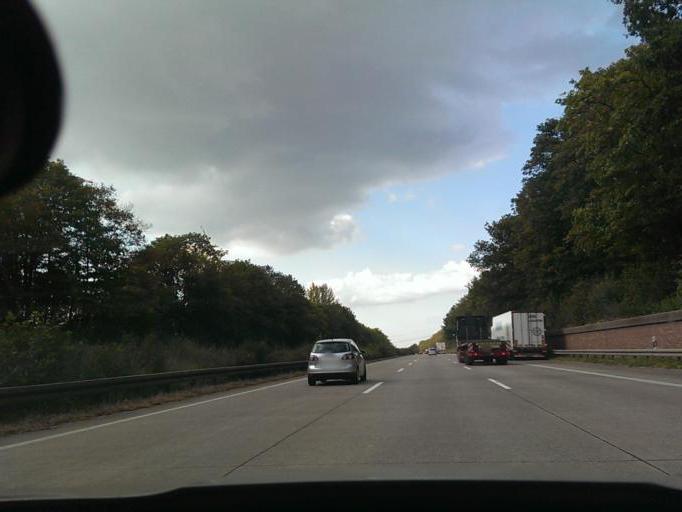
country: DE
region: Lower Saxony
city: Algermissen
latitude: 52.2653
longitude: 9.9159
